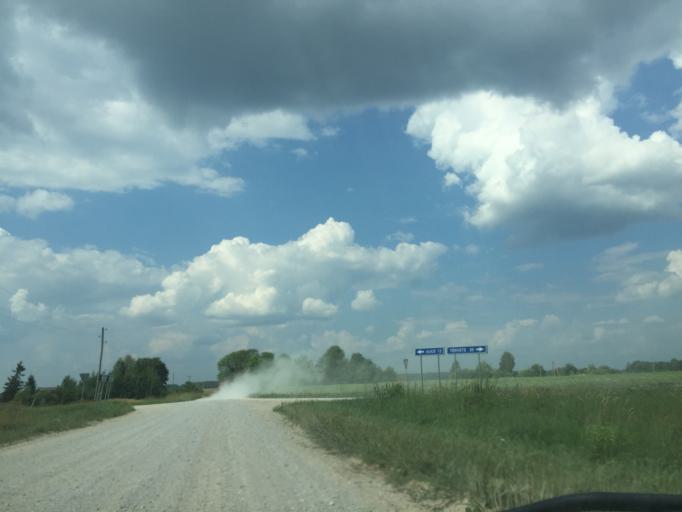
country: LV
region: Auces Novads
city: Auce
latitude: 56.4009
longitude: 23.0585
